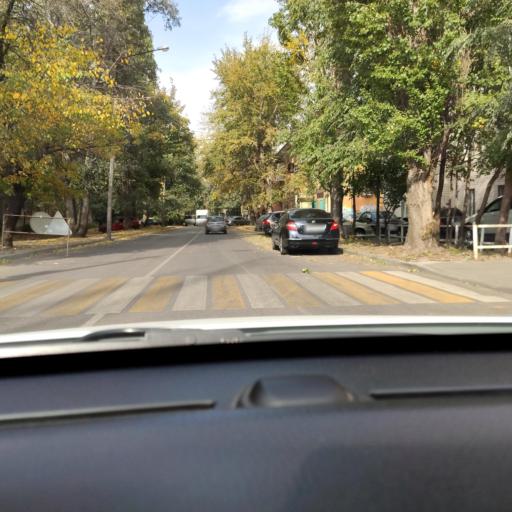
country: RU
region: Voronezj
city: Voronezh
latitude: 51.6826
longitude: 39.1955
